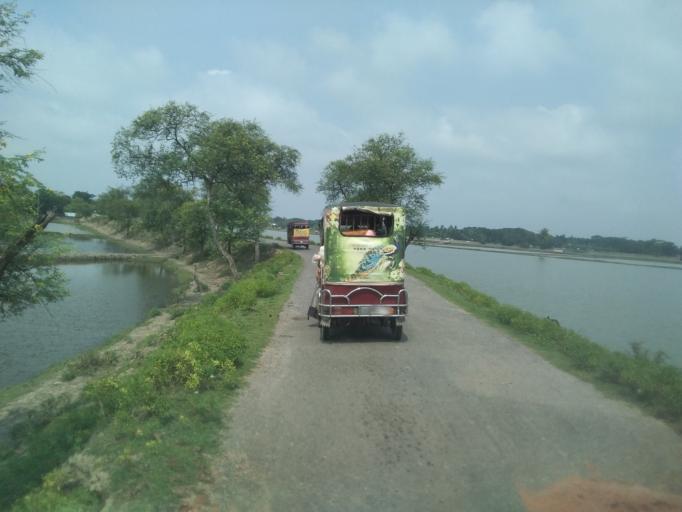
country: BD
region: Khulna
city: Phultala
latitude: 22.7051
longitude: 89.4602
